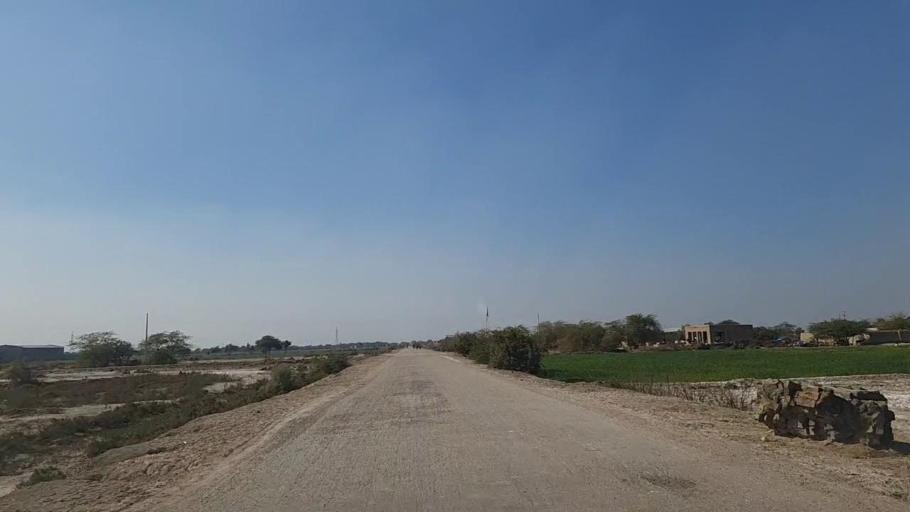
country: PK
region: Sindh
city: Daur
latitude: 26.3499
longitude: 68.3492
